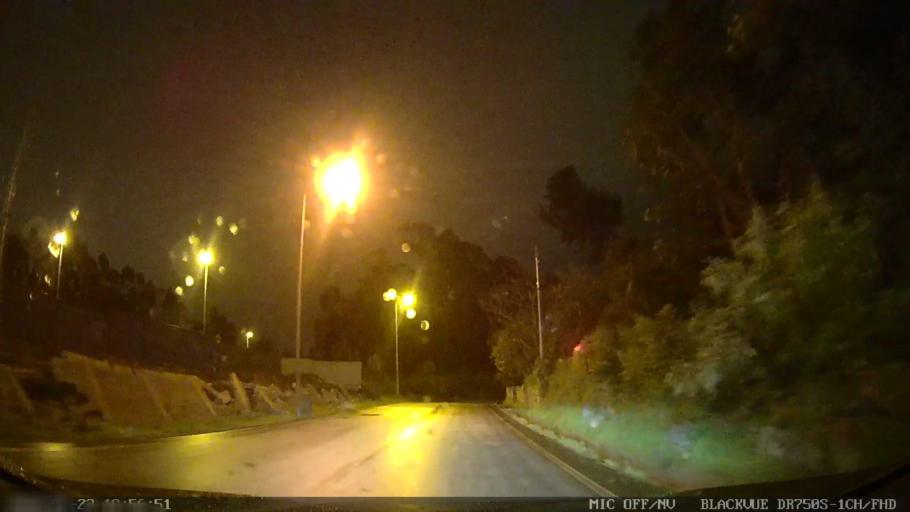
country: PT
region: Porto
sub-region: Matosinhos
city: Santa Cruz do Bispo
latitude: 41.2272
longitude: -8.6605
